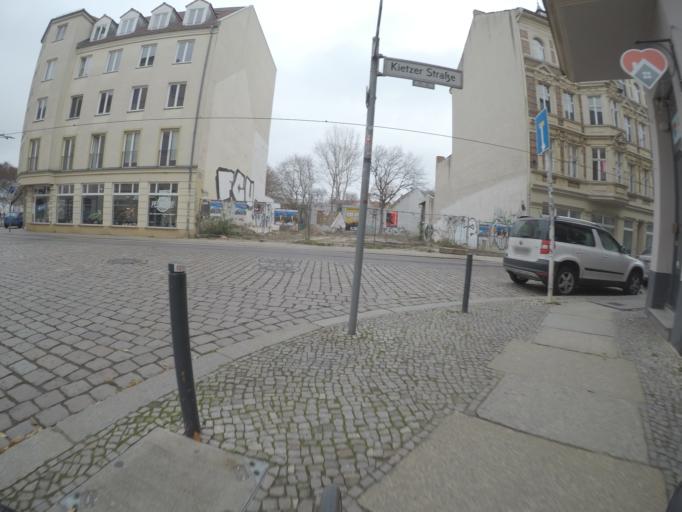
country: DE
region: Berlin
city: Kopenick Bezirk
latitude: 52.4451
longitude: 13.5771
